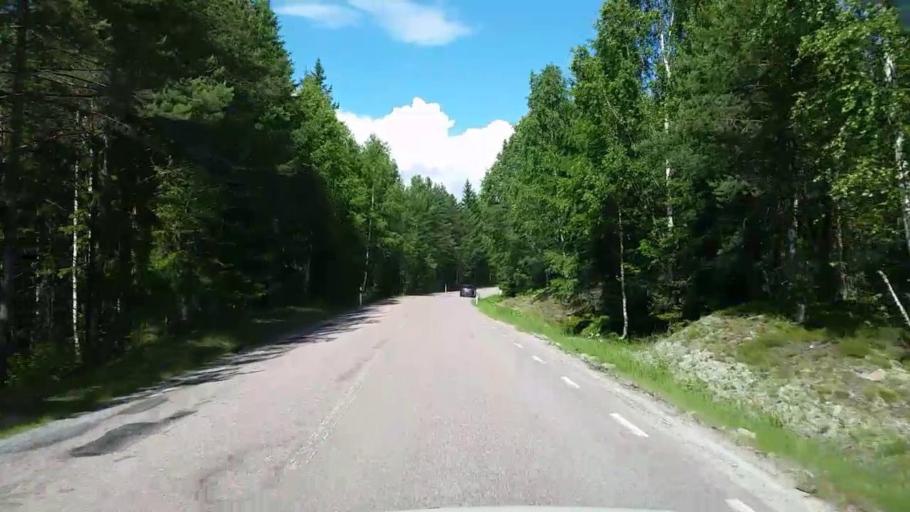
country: SE
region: Vaestmanland
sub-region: Fagersta Kommun
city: Fagersta
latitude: 59.9562
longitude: 15.7816
